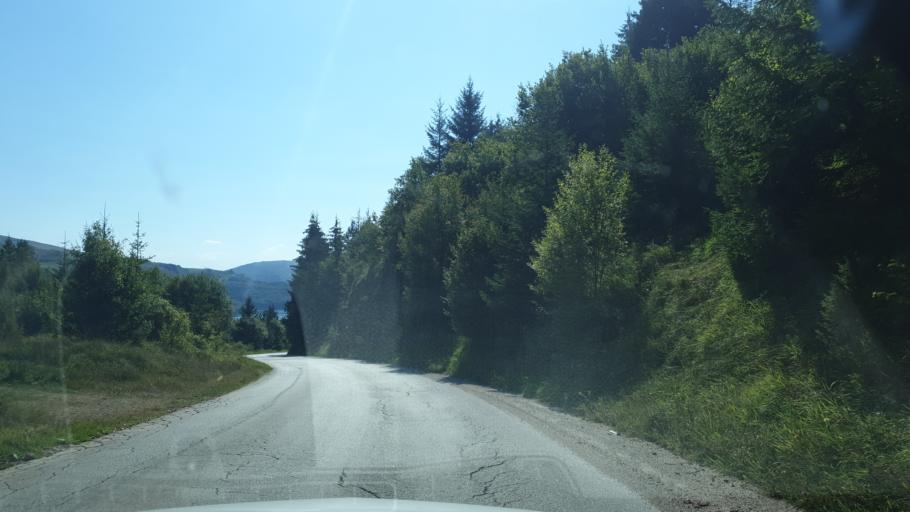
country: RS
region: Central Serbia
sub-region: Zlatiborski Okrug
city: Nova Varos
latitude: 43.4234
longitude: 19.9216
